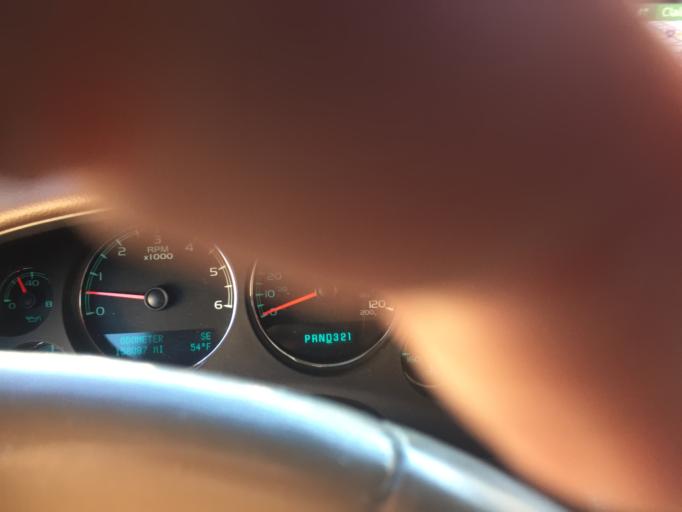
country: US
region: Louisiana
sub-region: Orleans Parish
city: New Orleans
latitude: 29.9778
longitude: -90.0694
